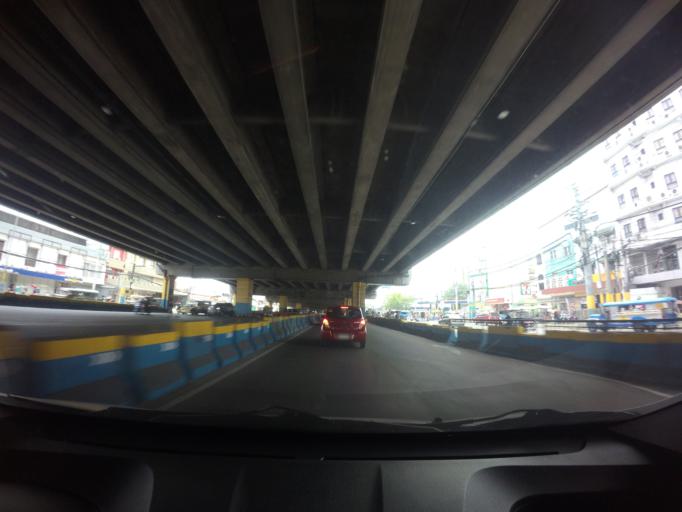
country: PH
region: Calabarzon
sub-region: Province of Laguna
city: San Pedro
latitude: 14.4189
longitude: 121.0458
